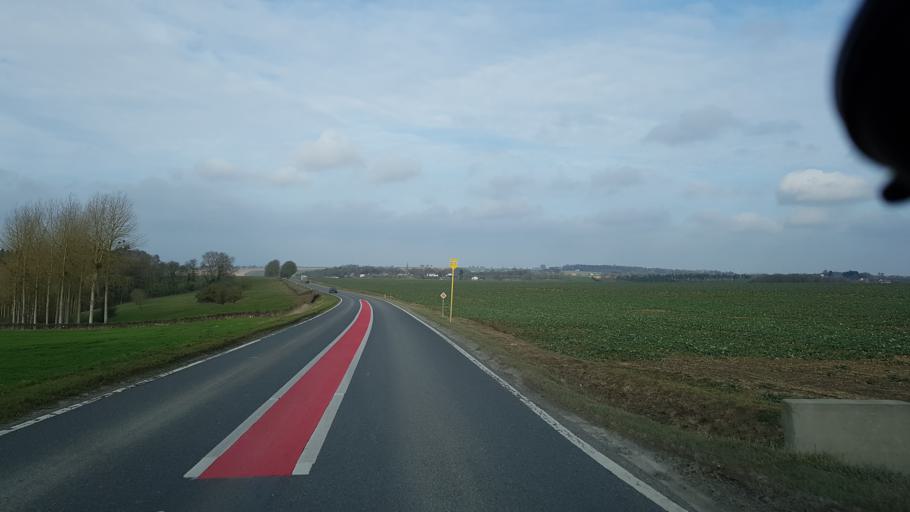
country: BE
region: Wallonia
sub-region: Province de Liege
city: Wanze
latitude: 50.5914
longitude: 5.2060
